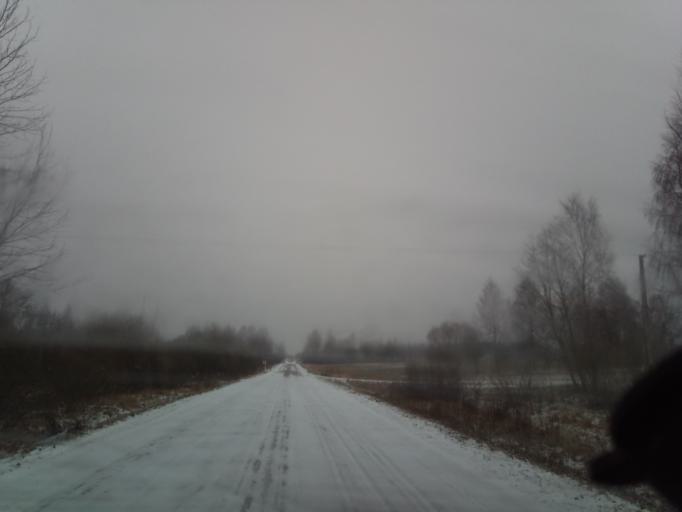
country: LT
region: Utenos apskritis
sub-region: Anyksciai
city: Anyksciai
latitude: 55.4062
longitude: 25.1105
